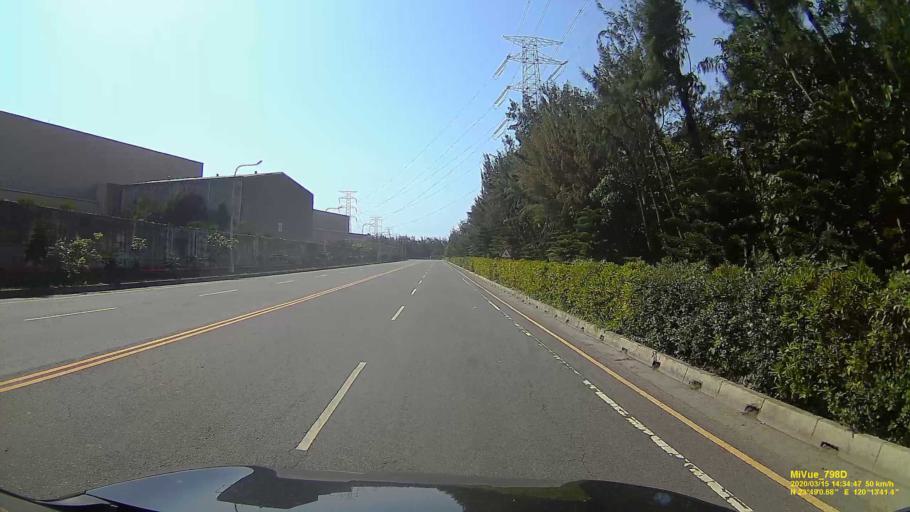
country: TW
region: Taiwan
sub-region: Yunlin
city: Douliu
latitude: 23.8169
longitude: 120.2280
